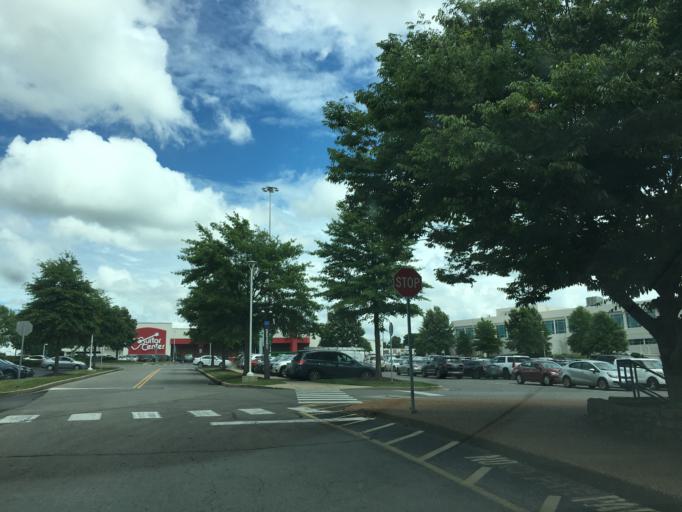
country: US
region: Tennessee
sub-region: Davidson County
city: Oak Hill
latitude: 36.1117
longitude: -86.7667
